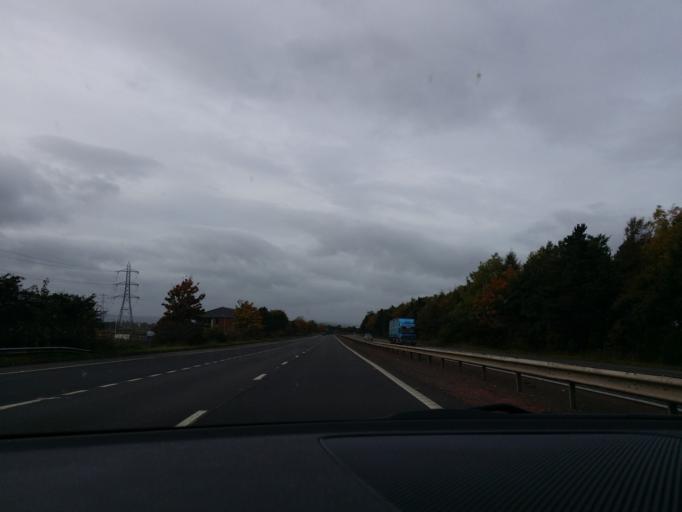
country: GB
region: Scotland
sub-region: Falkirk
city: Grangemouth
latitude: 55.9987
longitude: -3.7229
